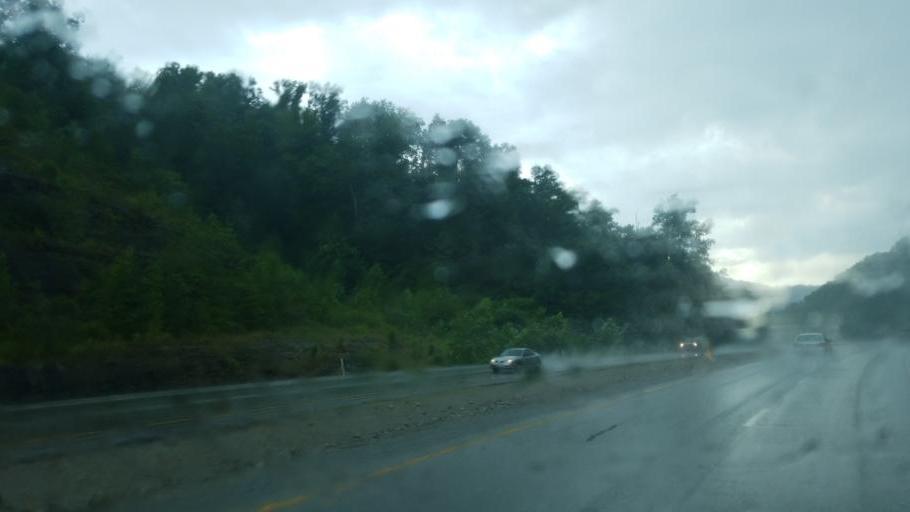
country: US
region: Kentucky
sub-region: Pike County
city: Pikeville
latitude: 37.5477
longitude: -82.4375
